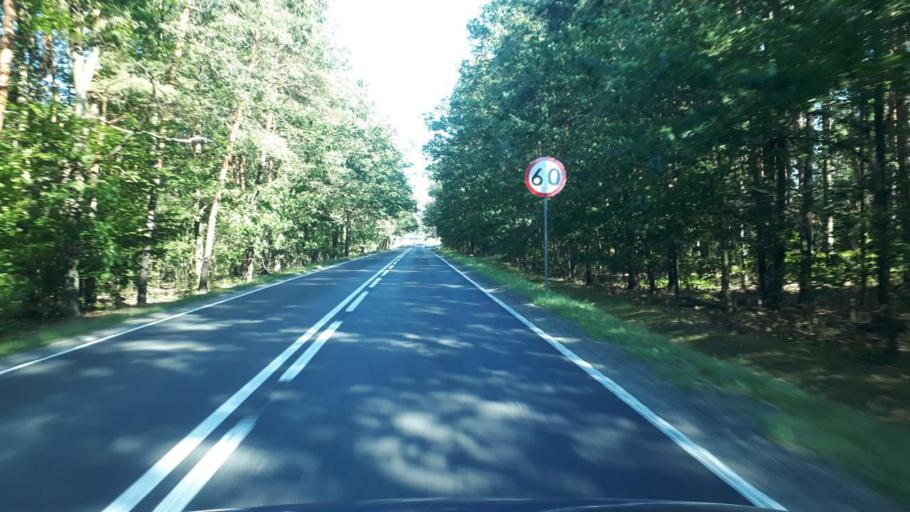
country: PL
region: Silesian Voivodeship
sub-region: Powiat lubliniecki
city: Sierakow Slaski
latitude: 50.8194
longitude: 18.5348
